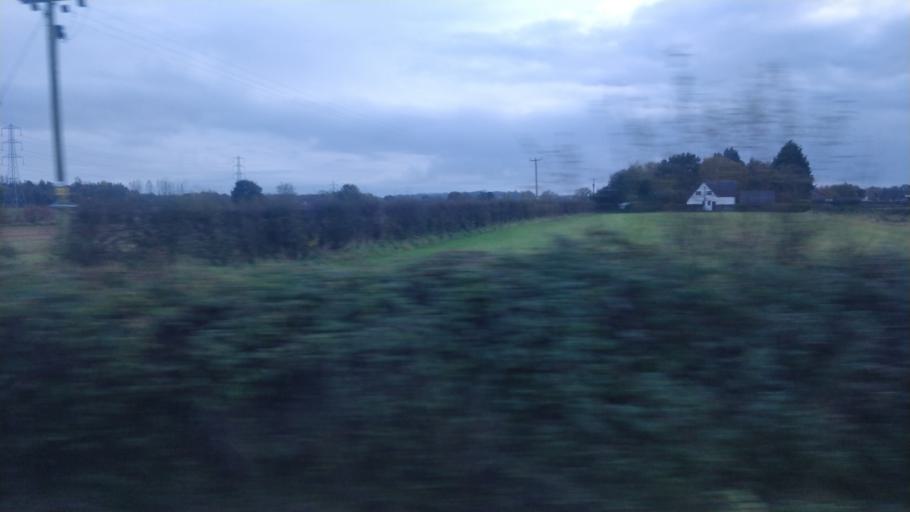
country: GB
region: England
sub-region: Lancashire
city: Parbold
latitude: 53.5970
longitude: -2.8009
